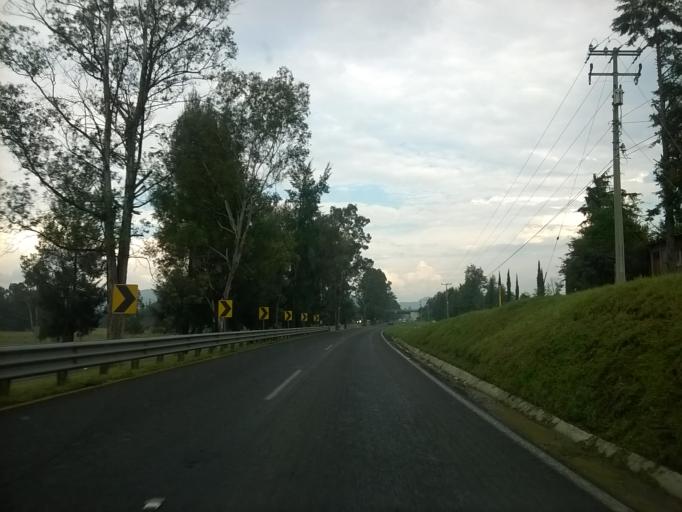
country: MX
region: Michoacan
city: Cuanajo
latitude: 19.5377
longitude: -101.5266
